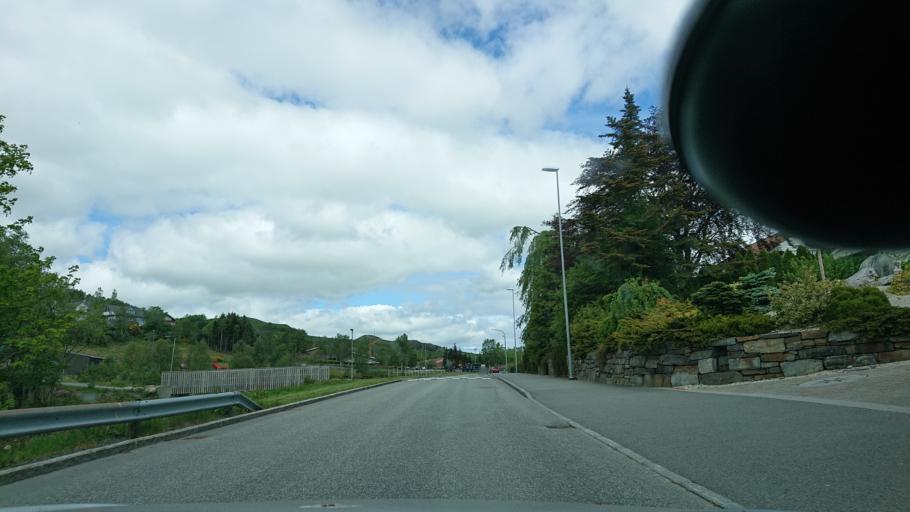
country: NO
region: Rogaland
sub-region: Gjesdal
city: Algard
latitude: 58.7704
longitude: 5.8652
